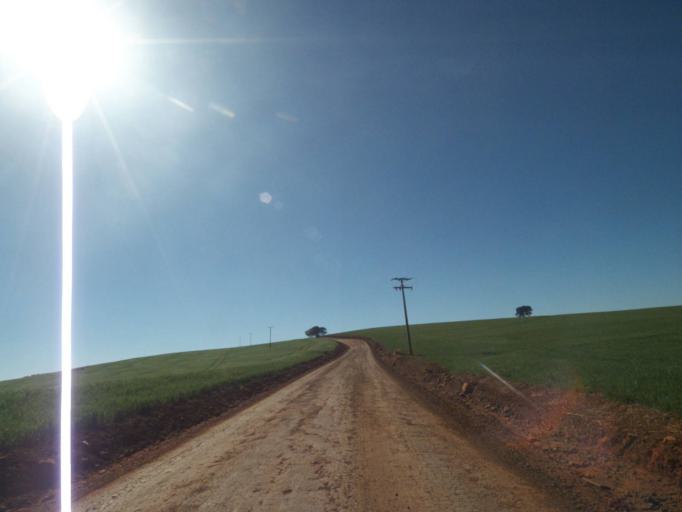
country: BR
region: Parana
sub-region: Tibagi
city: Tibagi
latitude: -24.6068
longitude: -50.6048
